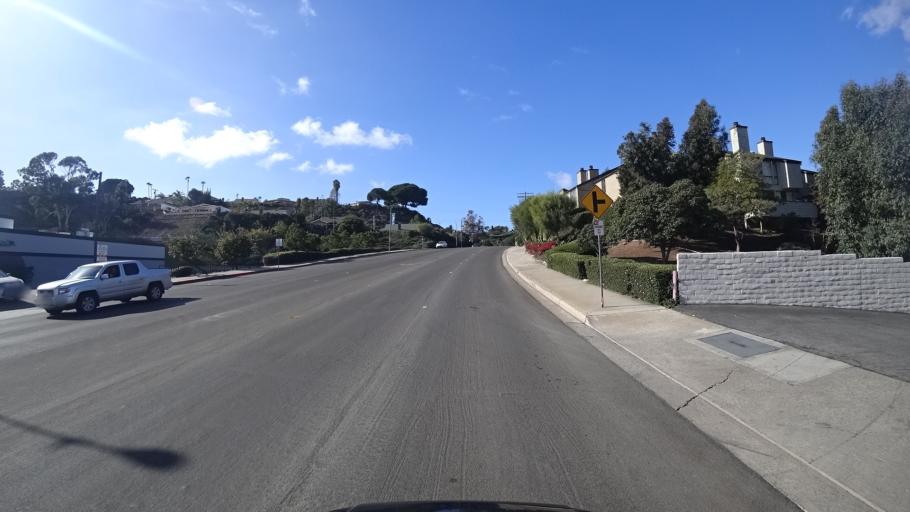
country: US
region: California
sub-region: Orange County
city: Dana Point
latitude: 33.4758
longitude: -117.6856
